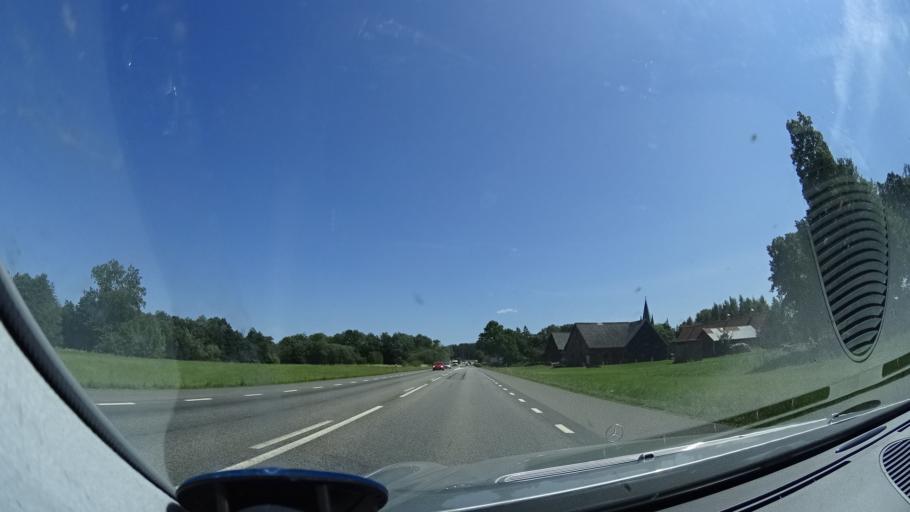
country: SE
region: Skane
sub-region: Kristianstads Kommun
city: Onnestad
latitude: 55.9294
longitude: 13.9622
